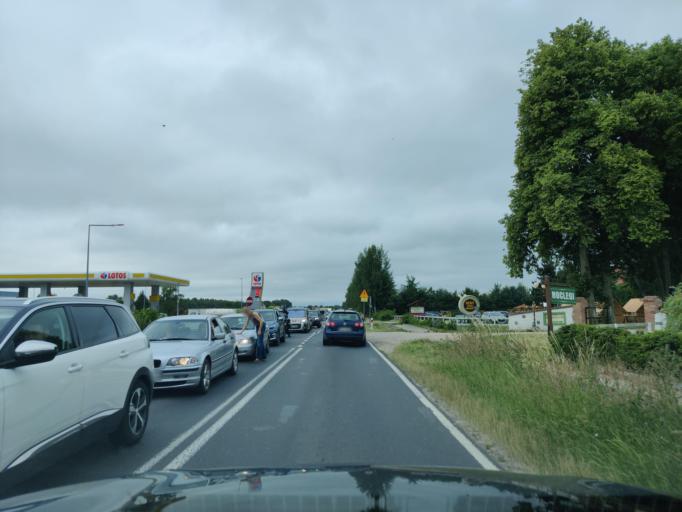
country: PL
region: Warmian-Masurian Voivodeship
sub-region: Powiat szczycienski
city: Rozogi
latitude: 53.4726
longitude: 21.3681
